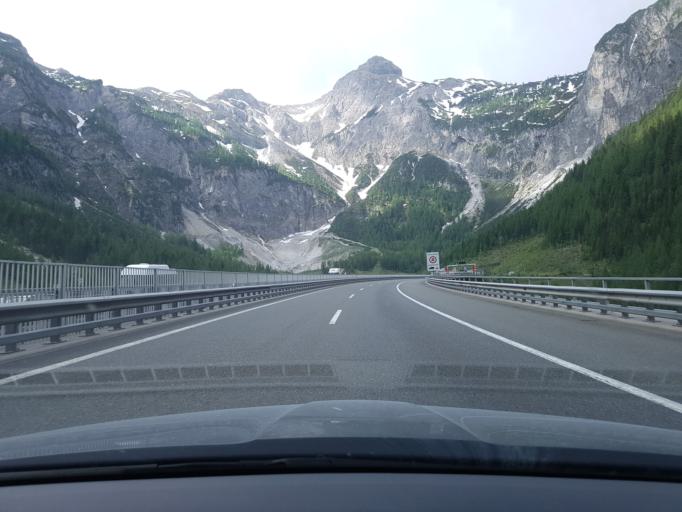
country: AT
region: Salzburg
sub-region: Politischer Bezirk Sankt Johann im Pongau
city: Untertauern
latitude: 47.2420
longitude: 13.4244
